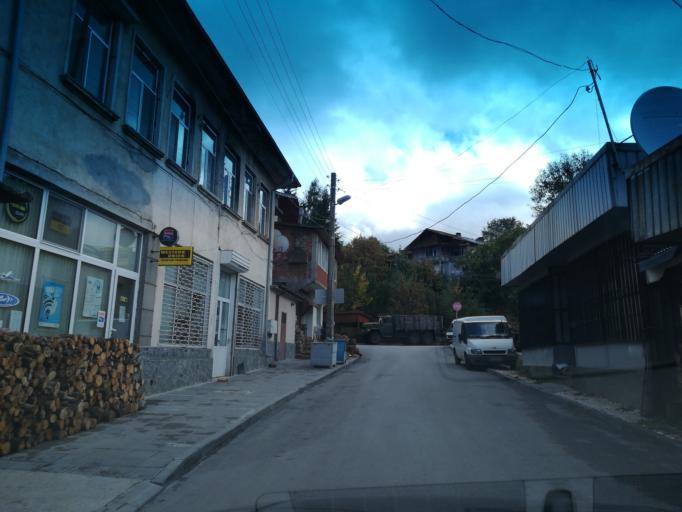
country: BG
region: Pazardzhik
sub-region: Obshtina Batak
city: Batak
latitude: 41.9364
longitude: 24.2692
